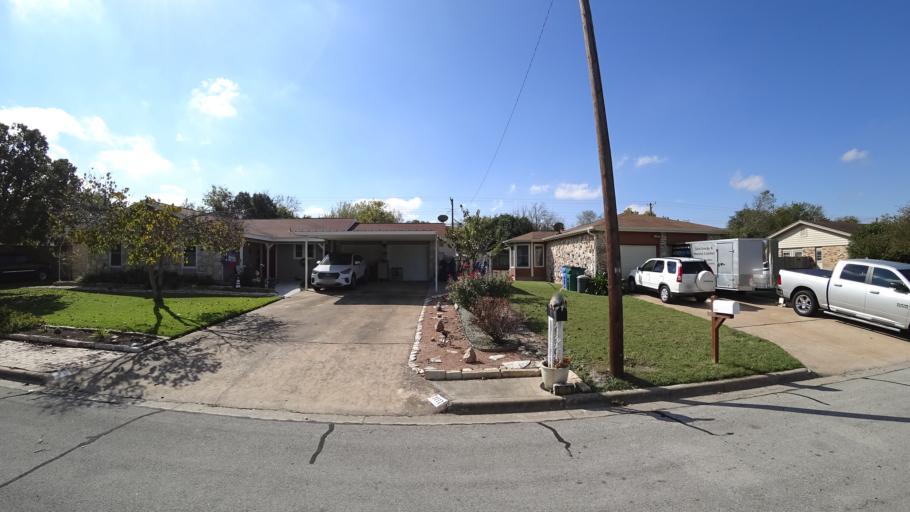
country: US
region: Texas
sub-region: Travis County
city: Windemere
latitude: 30.4588
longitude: -97.6471
